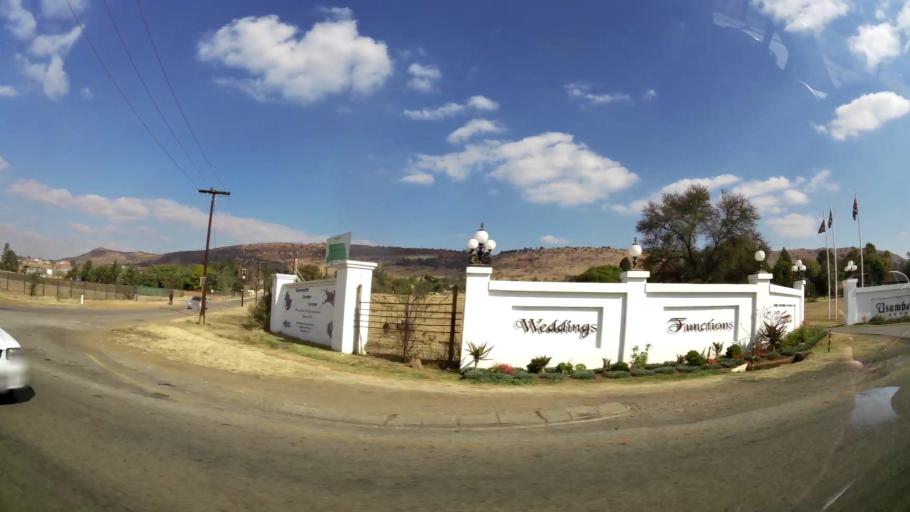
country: ZA
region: Gauteng
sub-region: West Rand District Municipality
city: Muldersdriseloop
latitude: -26.0523
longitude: 27.8134
